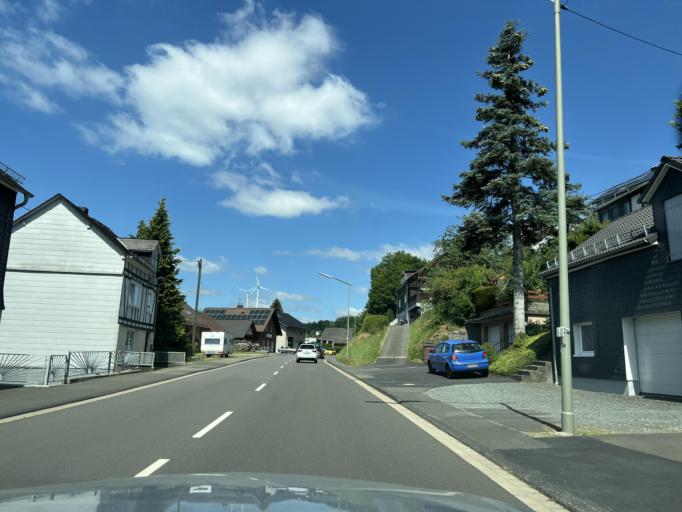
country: DE
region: North Rhine-Westphalia
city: Freudenberg
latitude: 50.9132
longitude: 7.8886
